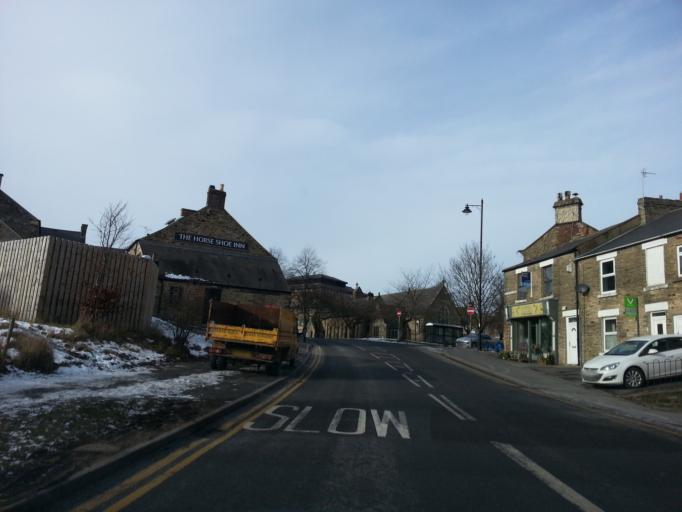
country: GB
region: England
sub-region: County Durham
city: Crook
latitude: 54.7149
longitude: -1.7422
